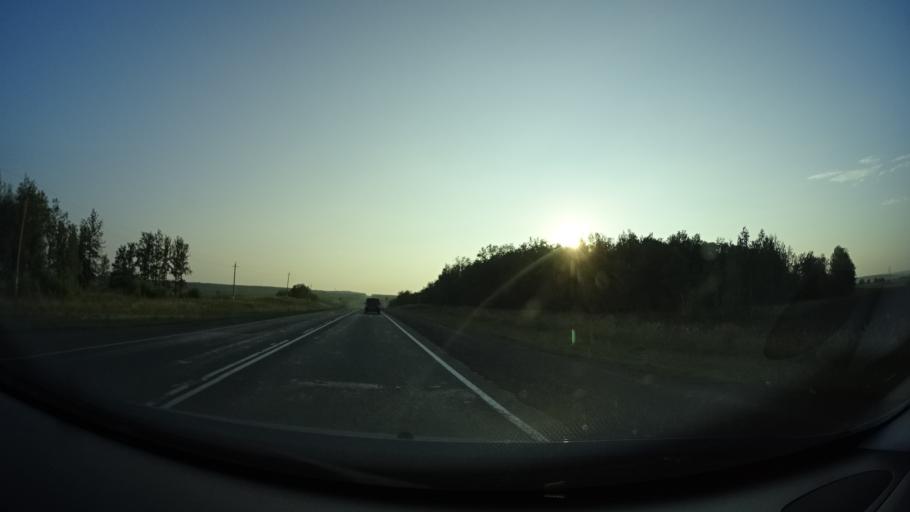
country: RU
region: Samara
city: Isakly
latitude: 54.0141
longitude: 51.7272
